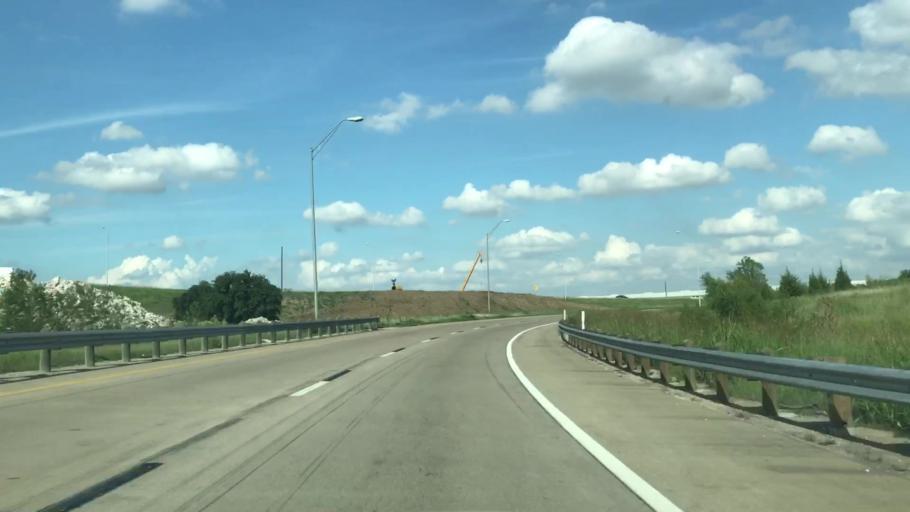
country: US
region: Texas
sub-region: Dallas County
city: Coppell
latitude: 32.9477
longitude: -97.0382
